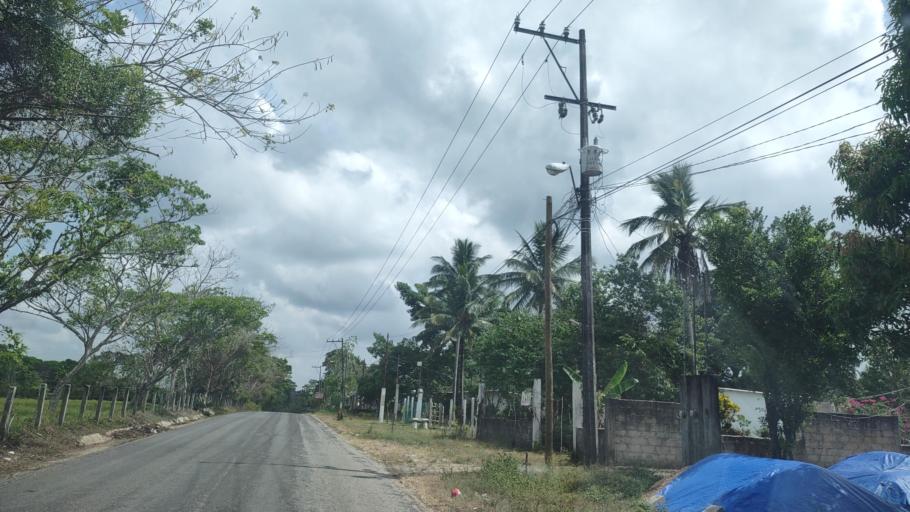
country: MX
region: Veracruz
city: Las Choapas
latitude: 17.9504
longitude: -94.1099
